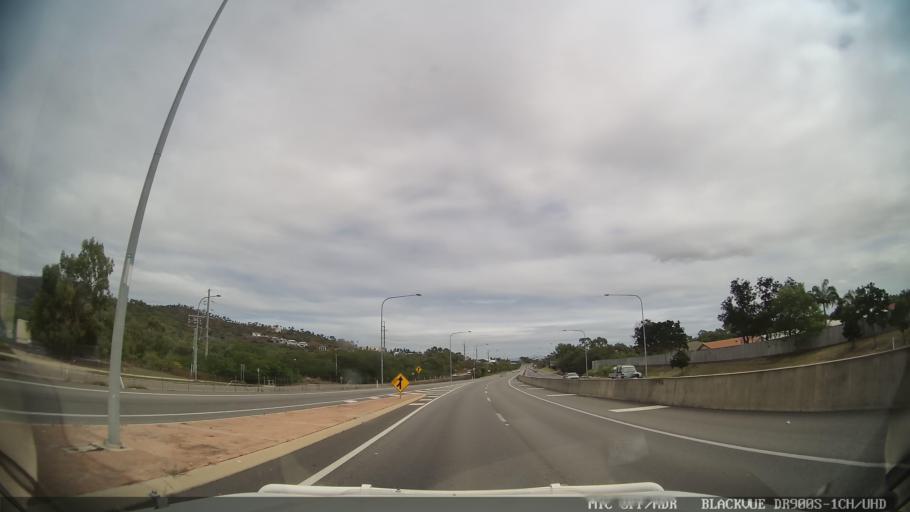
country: AU
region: Queensland
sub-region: Townsville
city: Bohle Plains
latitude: -19.3209
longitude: 146.7555
